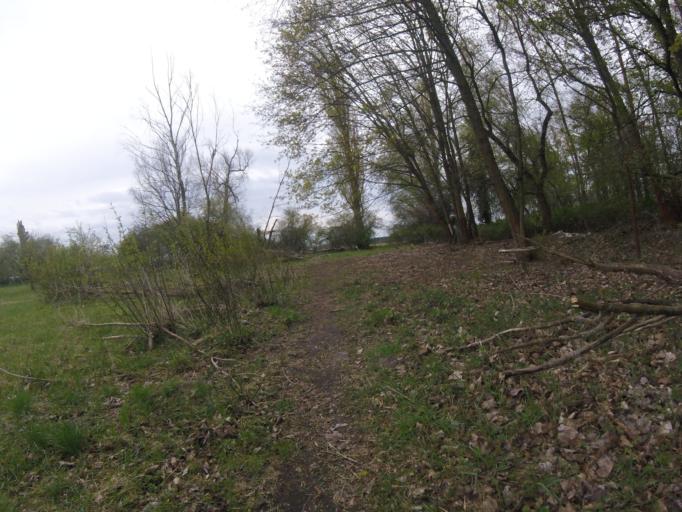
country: DE
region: Brandenburg
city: Bestensee
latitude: 52.2368
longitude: 13.6758
